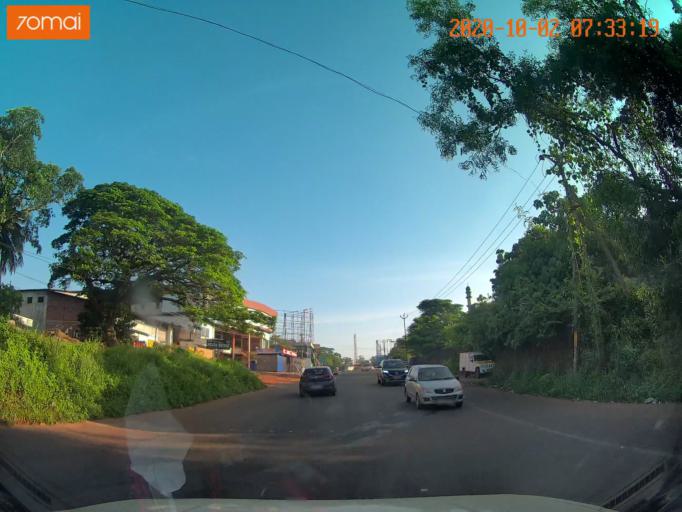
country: IN
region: Kerala
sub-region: Malappuram
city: Pariyapuram
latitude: 11.0580
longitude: 75.9354
